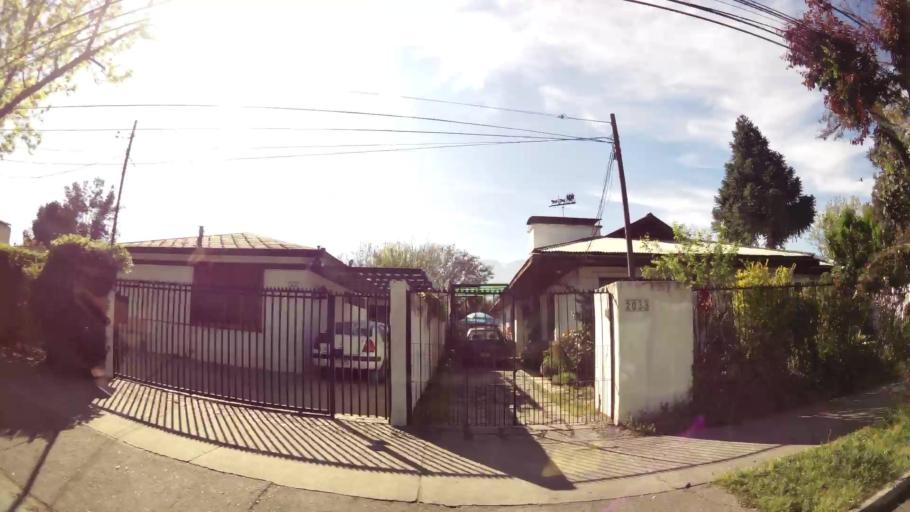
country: CL
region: Santiago Metropolitan
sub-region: Provincia de Santiago
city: Villa Presidente Frei, Nunoa, Santiago, Chile
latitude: -33.4359
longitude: -70.5576
